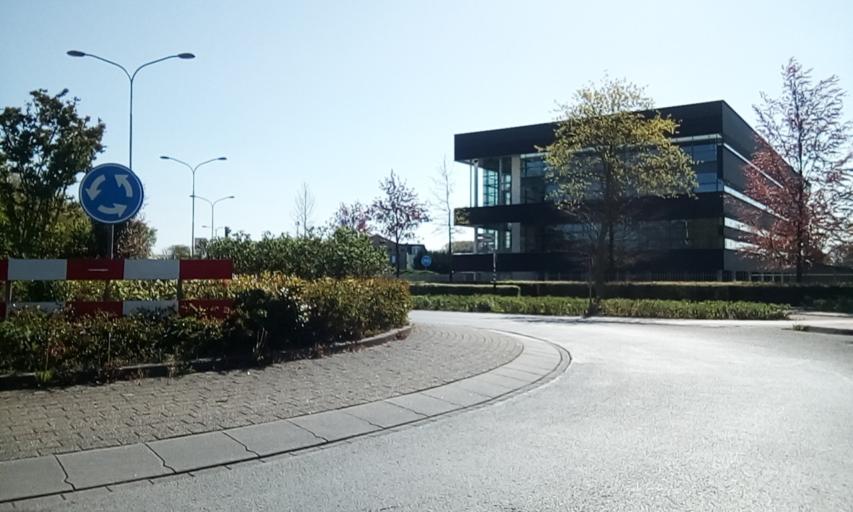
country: NL
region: Gelderland
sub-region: Gemeente Druten
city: Druten
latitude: 51.8856
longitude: 5.6047
